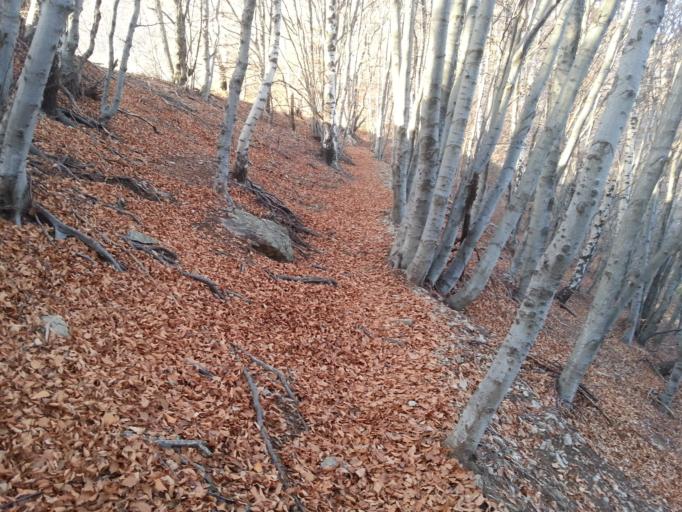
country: IT
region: Lombardy
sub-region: Provincia di Varese
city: Curiglia
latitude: 46.0327
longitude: 8.8442
